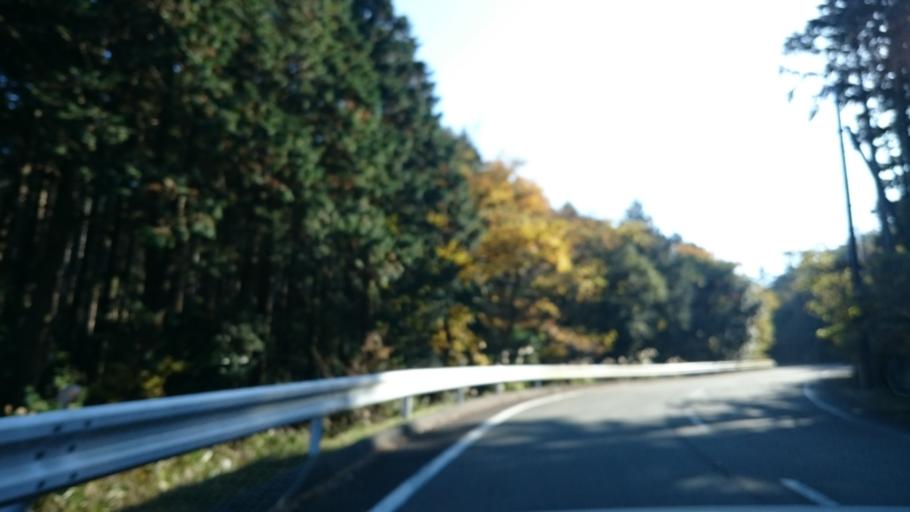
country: JP
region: Shizuoka
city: Heda
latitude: 34.9908
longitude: 138.8113
